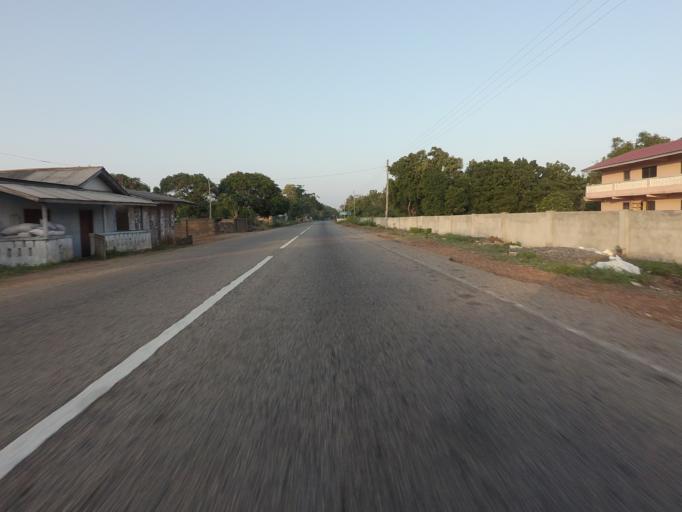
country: GH
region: Volta
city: Anloga
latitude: 5.7898
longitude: 0.8663
